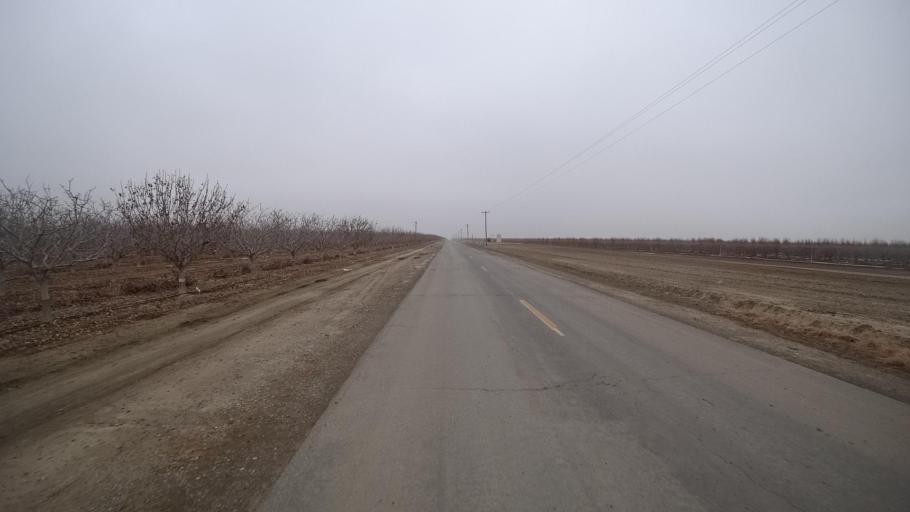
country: US
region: California
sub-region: Kern County
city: Wasco
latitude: 35.6466
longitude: -119.5088
